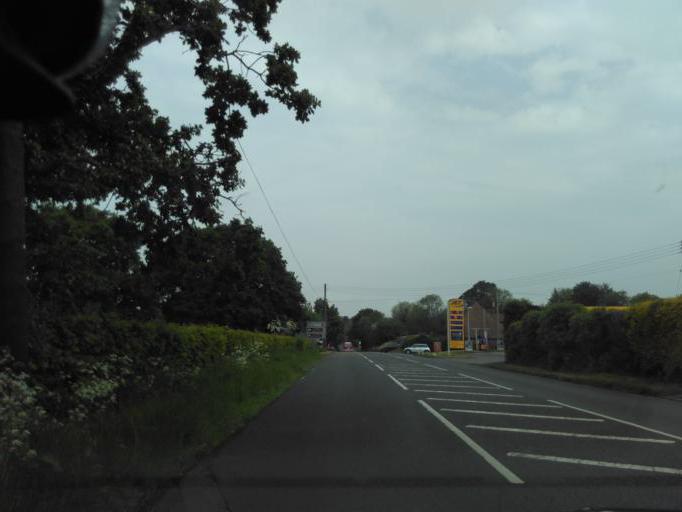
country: GB
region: England
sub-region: Kent
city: Lyminge
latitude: 51.1573
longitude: 1.0512
